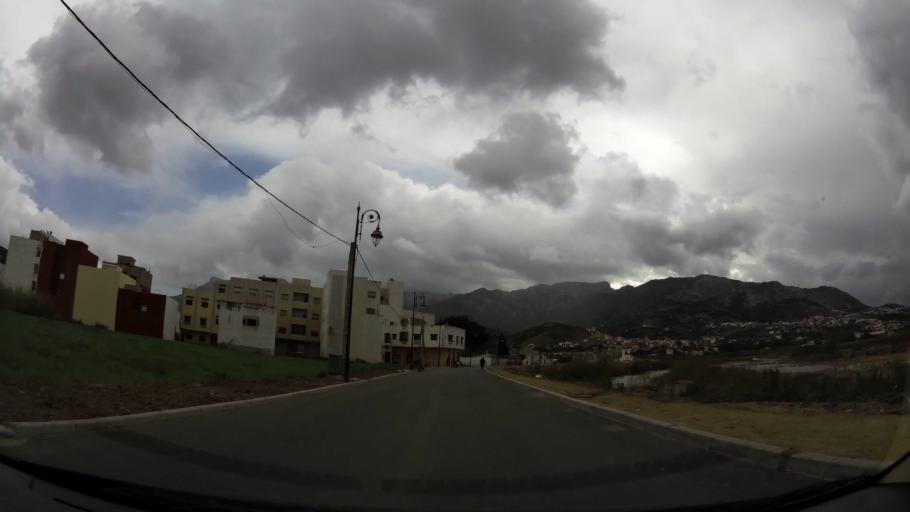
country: MA
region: Tanger-Tetouan
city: Tetouan
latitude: 35.5604
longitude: -5.3498
